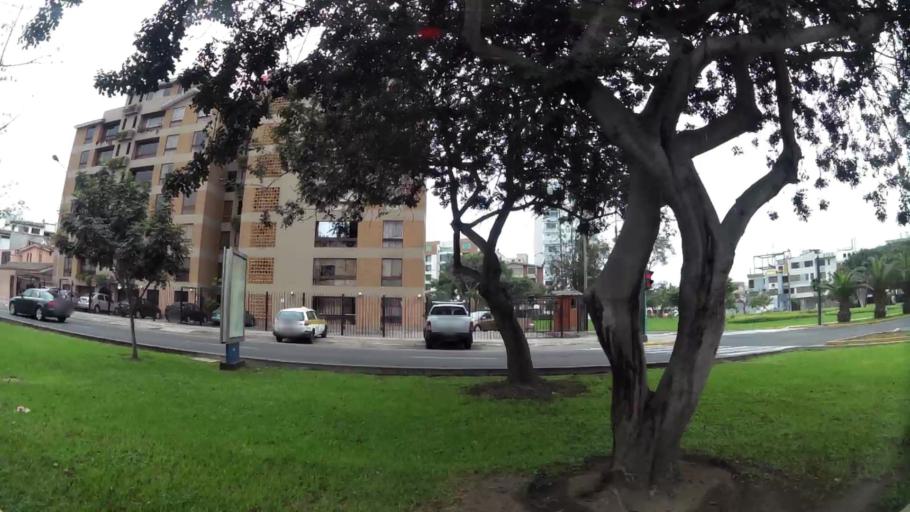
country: PE
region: Lima
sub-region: Lima
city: San Luis
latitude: -12.1027
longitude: -77.0115
